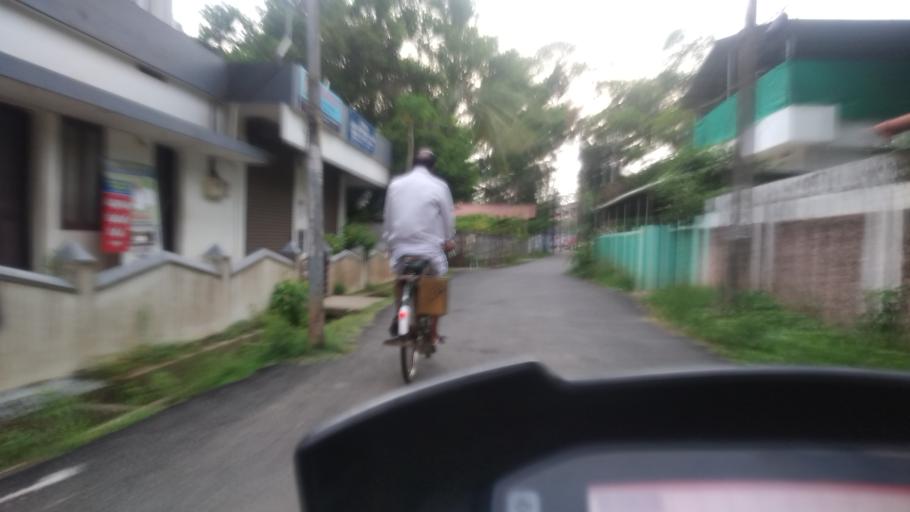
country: IN
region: Kerala
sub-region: Ernakulam
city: Elur
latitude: 10.0669
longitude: 76.2143
